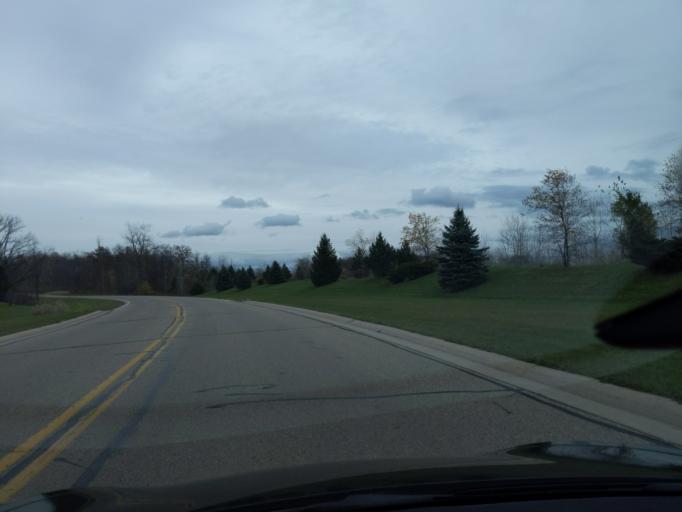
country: US
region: Michigan
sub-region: Ingham County
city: Lansing
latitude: 42.7758
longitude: -84.5396
